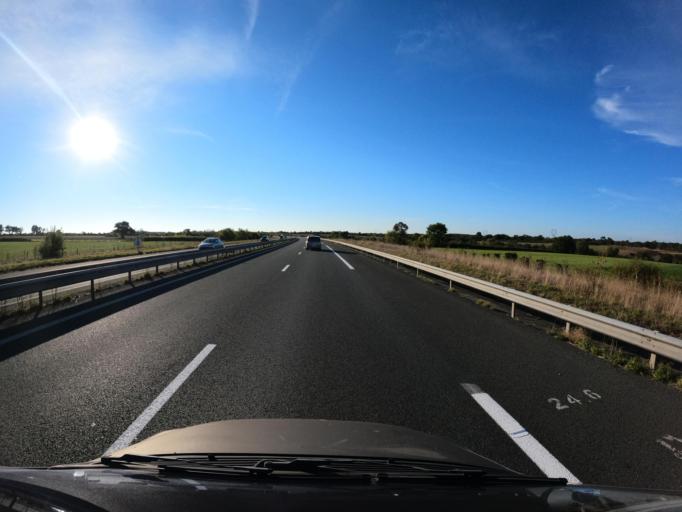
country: FR
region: Pays de la Loire
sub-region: Departement de Maine-et-Loire
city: Chemille-Melay
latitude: 47.2472
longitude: -0.6923
